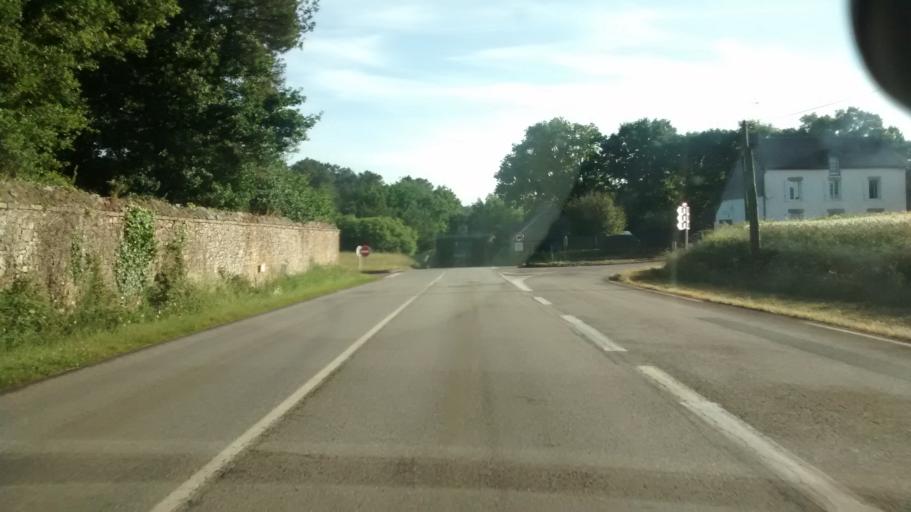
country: FR
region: Brittany
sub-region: Departement du Morbihan
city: Molac
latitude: 47.7684
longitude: -2.4341
